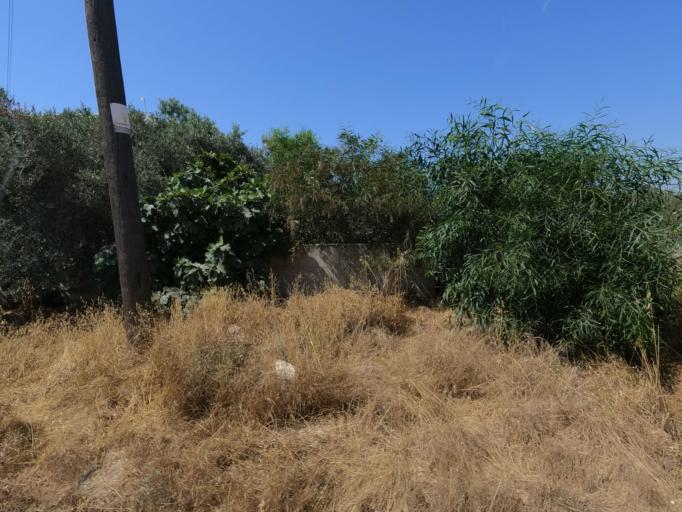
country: CY
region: Ammochostos
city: Paralimni
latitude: 35.0057
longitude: 33.9713
